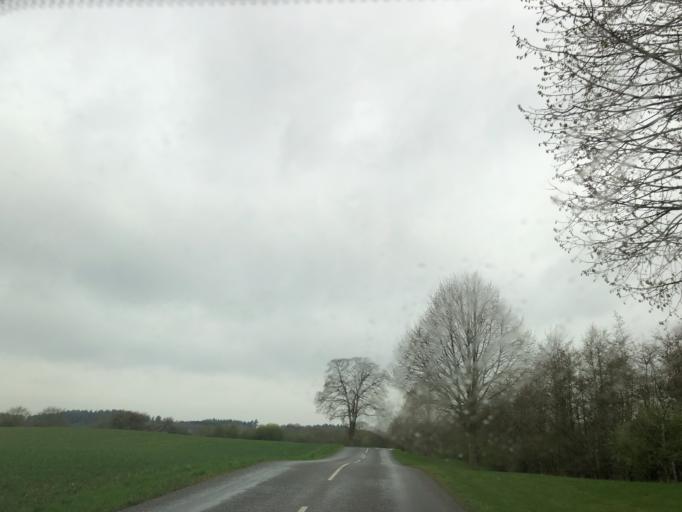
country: DK
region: Zealand
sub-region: Lejre Kommune
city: Kirke Hvalso
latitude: 55.5289
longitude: 11.8549
